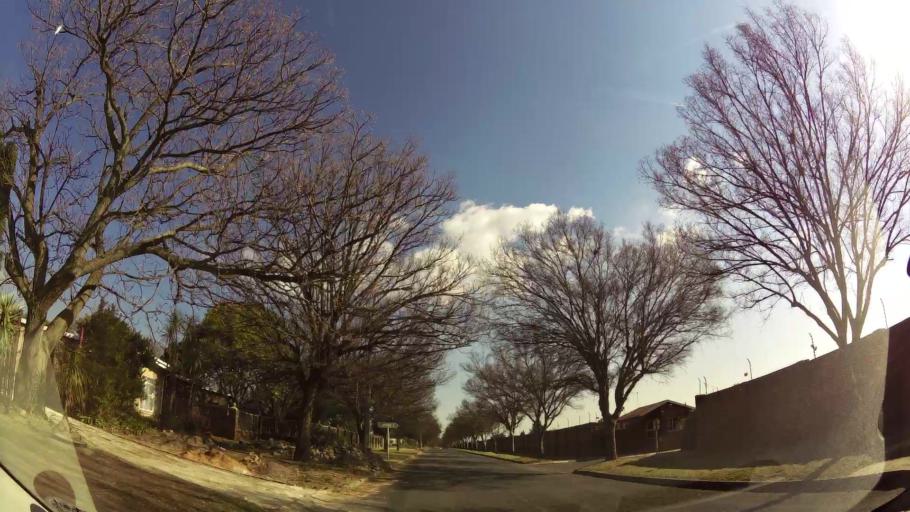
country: ZA
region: Gauteng
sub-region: Ekurhuleni Metropolitan Municipality
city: Benoni
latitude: -26.1395
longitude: 28.3455
